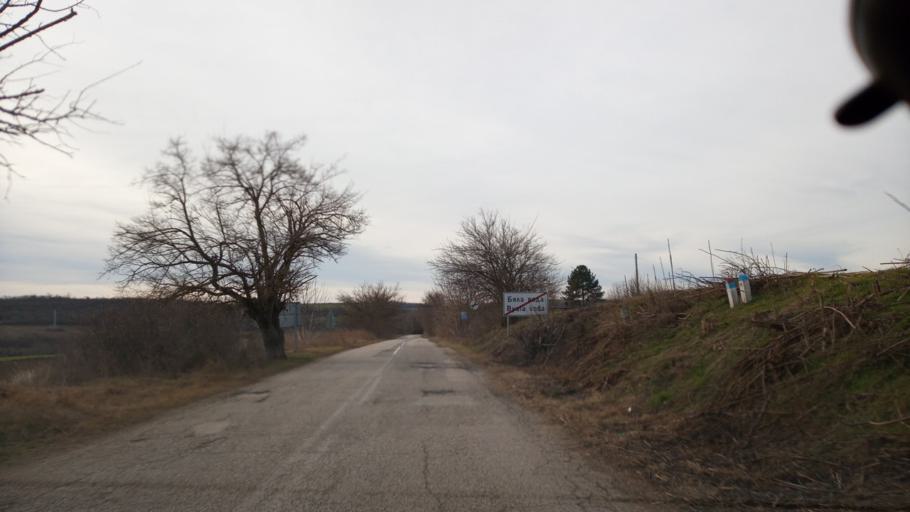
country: BG
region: Pleven
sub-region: Obshtina Belene
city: Belene
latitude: 43.6260
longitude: 25.0390
